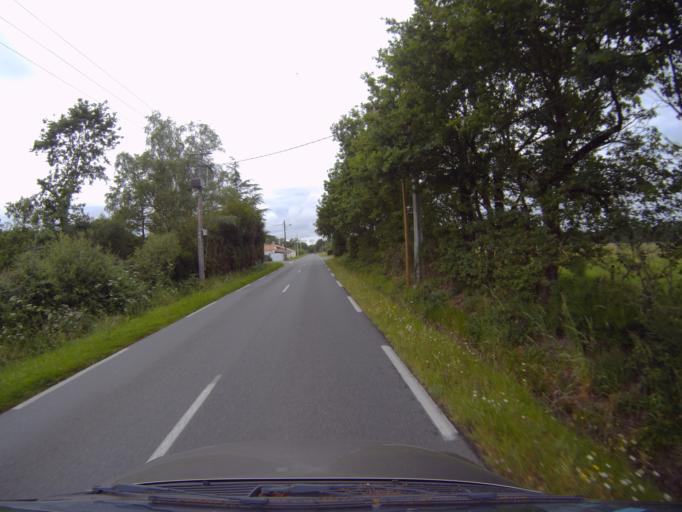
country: FR
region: Pays de la Loire
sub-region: Departement de la Loire-Atlantique
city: Geneston
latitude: 47.0619
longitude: -1.5520
